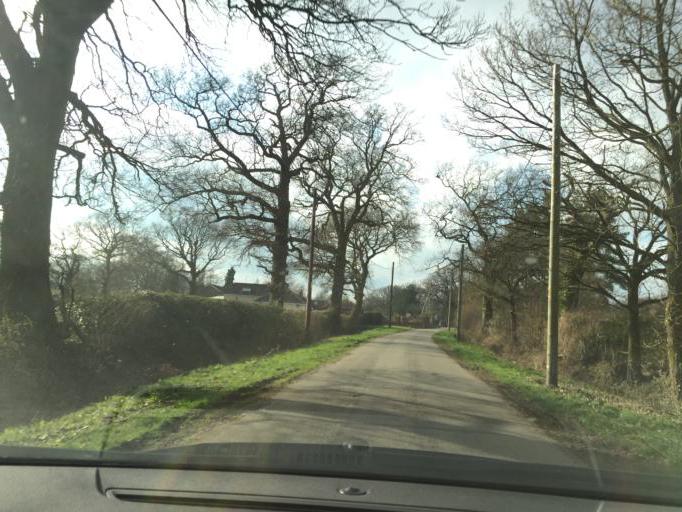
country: GB
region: England
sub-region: Coventry
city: Keresley
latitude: 52.4421
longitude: -1.5853
